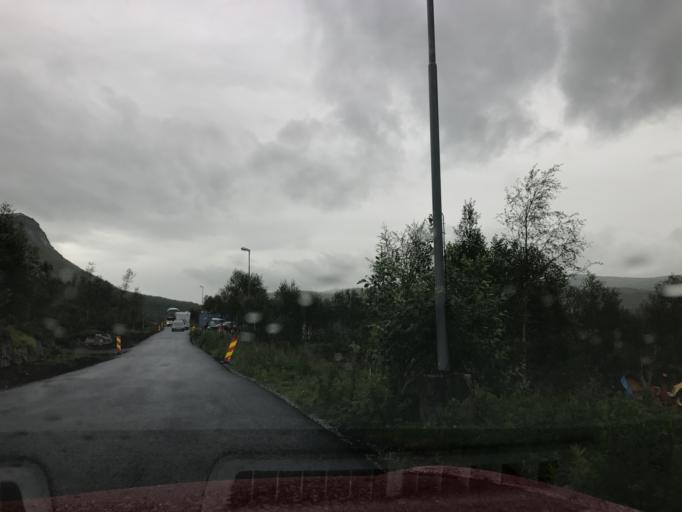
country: NO
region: Hordaland
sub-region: Eidfjord
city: Eidfjord
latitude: 60.4267
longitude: 7.2553
